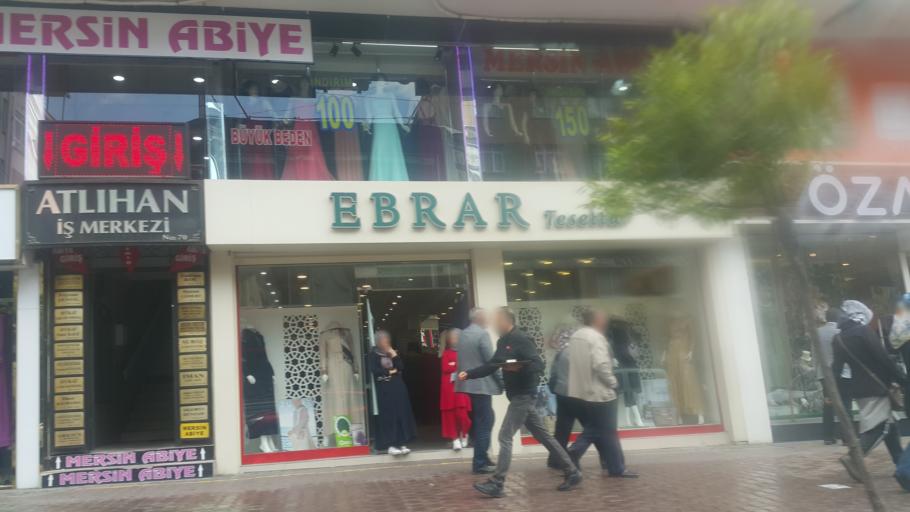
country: TR
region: Mersin
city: Mercin
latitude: 36.8023
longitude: 34.6256
